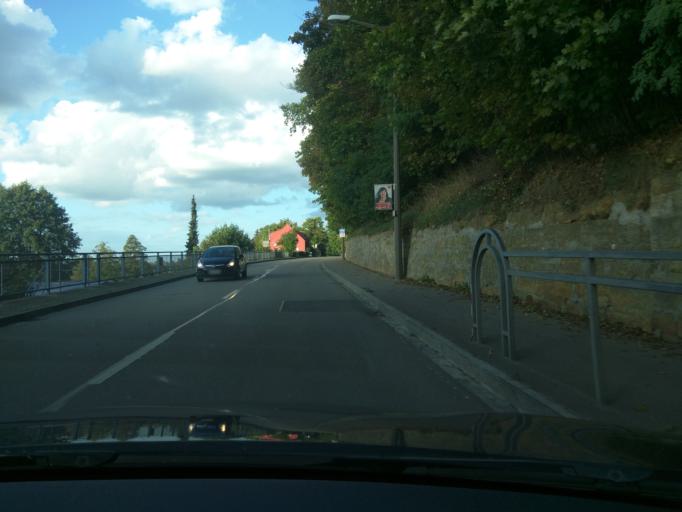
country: DE
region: Bavaria
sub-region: Upper Palatinate
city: Schwandorf in Bayern
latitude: 49.3334
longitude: 12.1103
